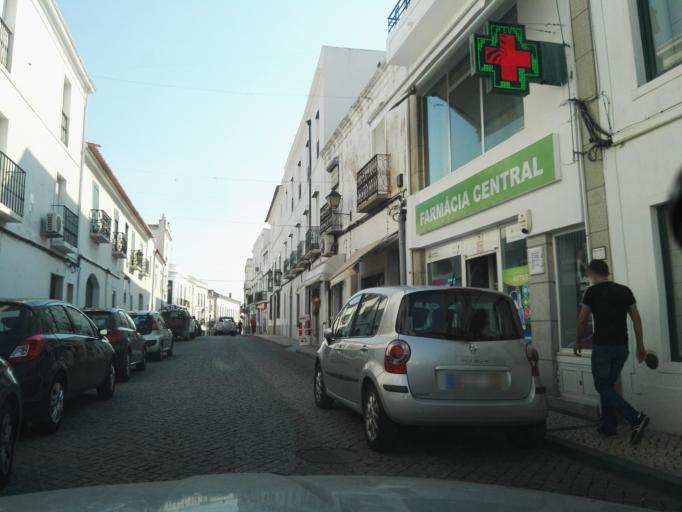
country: PT
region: Portalegre
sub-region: Campo Maior
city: Campo Maior
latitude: 39.0137
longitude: -7.0689
